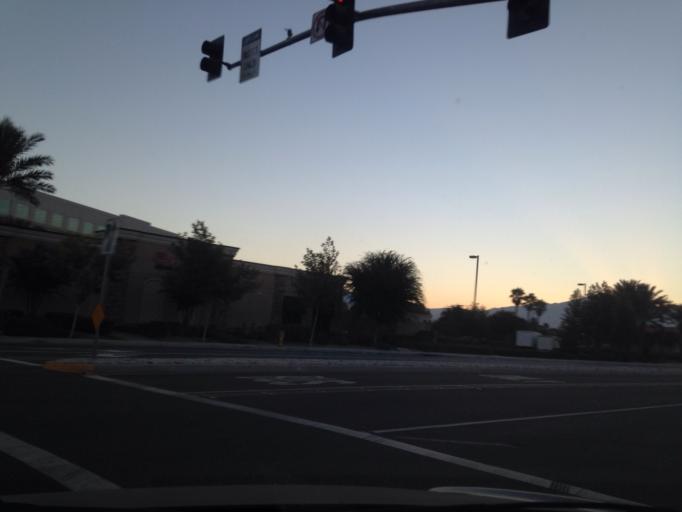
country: US
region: California
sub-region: San Bernardino County
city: Loma Linda
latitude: 34.0690
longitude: -117.2646
